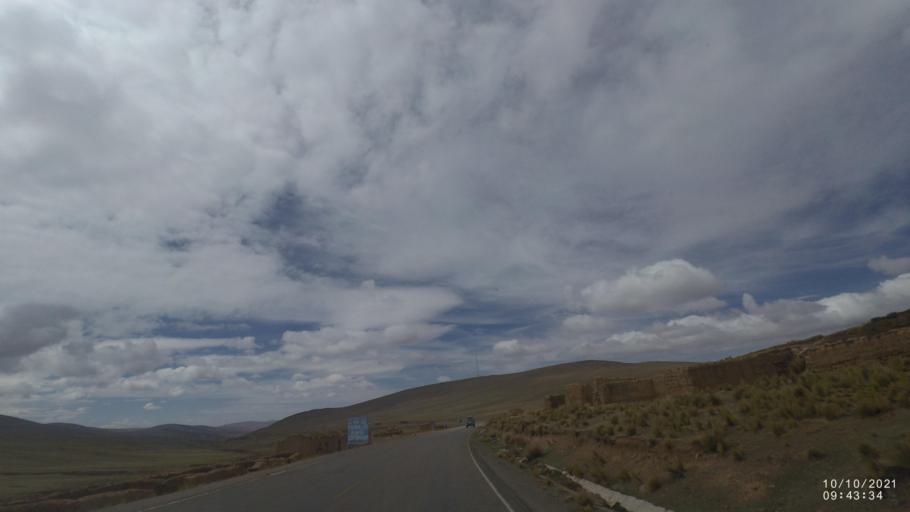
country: BO
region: La Paz
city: Quime
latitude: -17.1511
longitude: -67.3448
